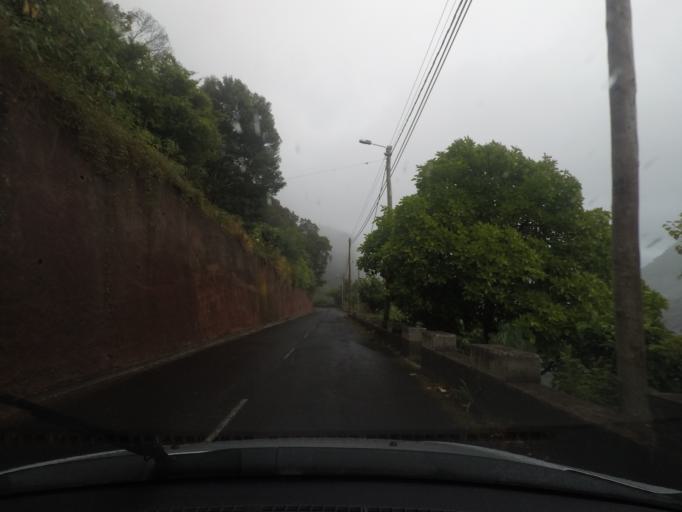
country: PT
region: Madeira
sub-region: Santana
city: Santana
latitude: 32.7796
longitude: -16.8623
